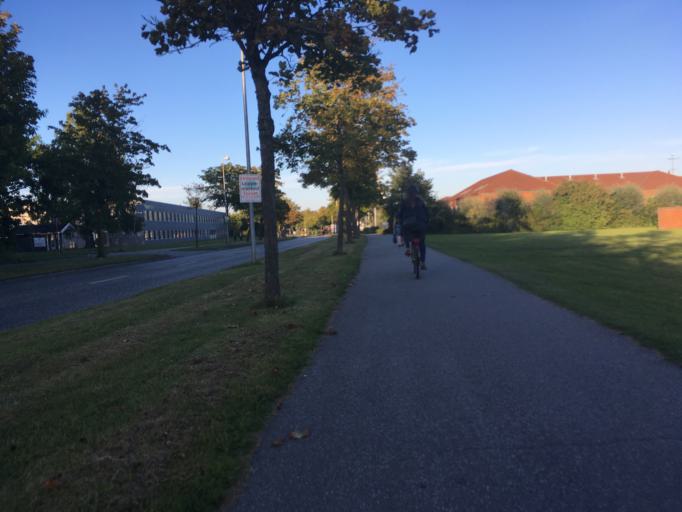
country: DK
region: Capital Region
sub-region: Hillerod Kommune
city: Hillerod
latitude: 55.9207
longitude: 12.2933
